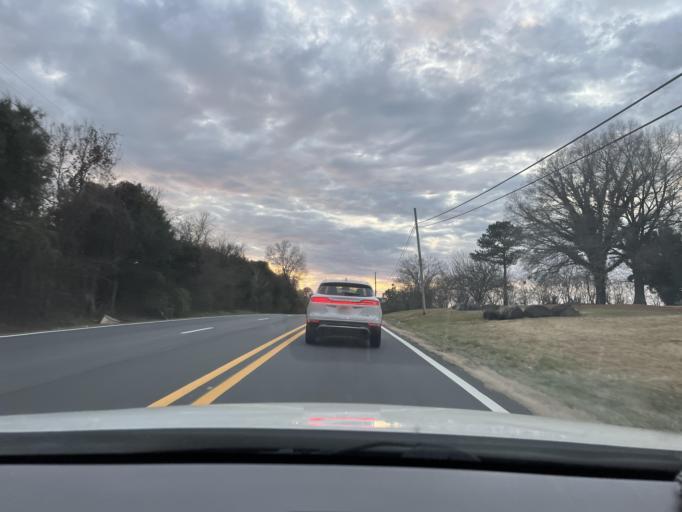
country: US
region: North Carolina
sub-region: Guilford County
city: Gibsonville
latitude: 36.0725
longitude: -79.5783
